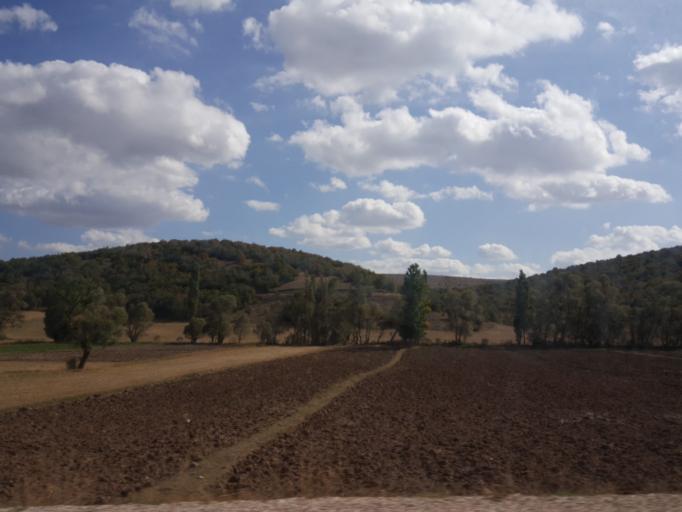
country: TR
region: Tokat
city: Camlibel
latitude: 40.1615
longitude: 36.4140
